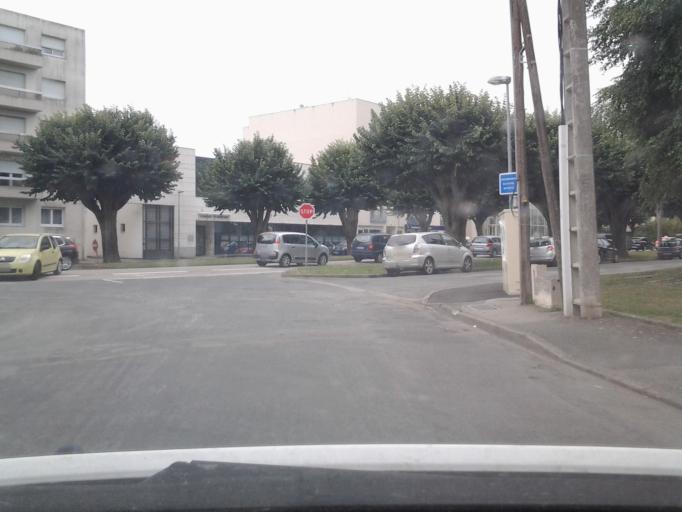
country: FR
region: Pays de la Loire
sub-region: Departement de la Vendee
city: La Roche-sur-Yon
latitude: 46.6654
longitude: -1.4215
